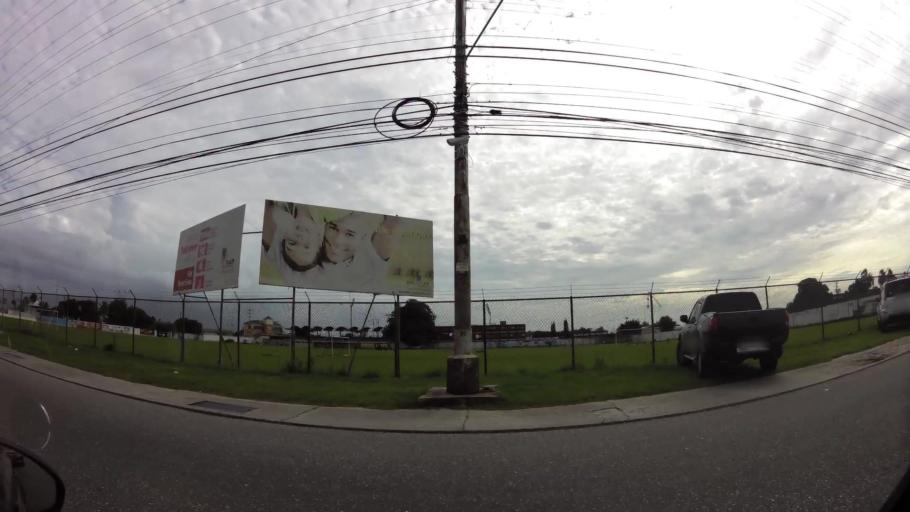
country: TT
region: City of Port of Spain
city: Mucurapo
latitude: 10.6668
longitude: -61.5316
